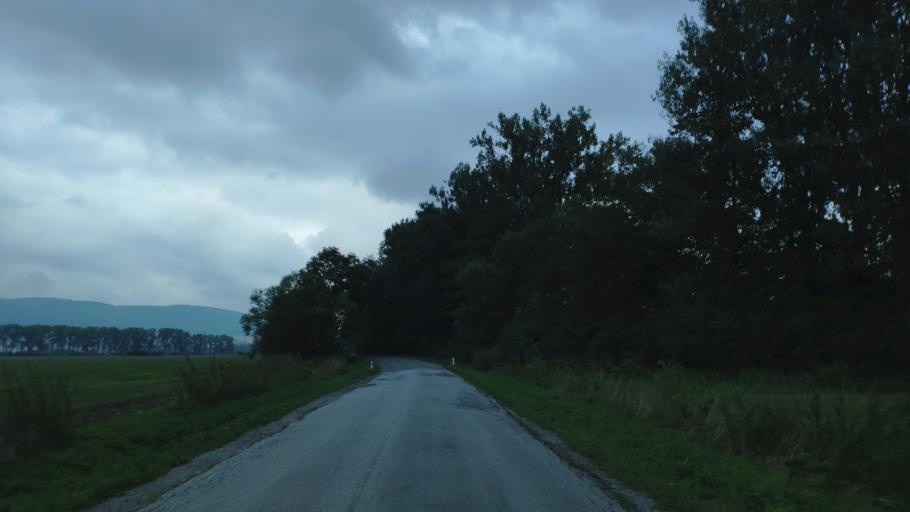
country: SK
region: Kosicky
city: Moldava nad Bodvou
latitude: 48.5861
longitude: 20.8944
